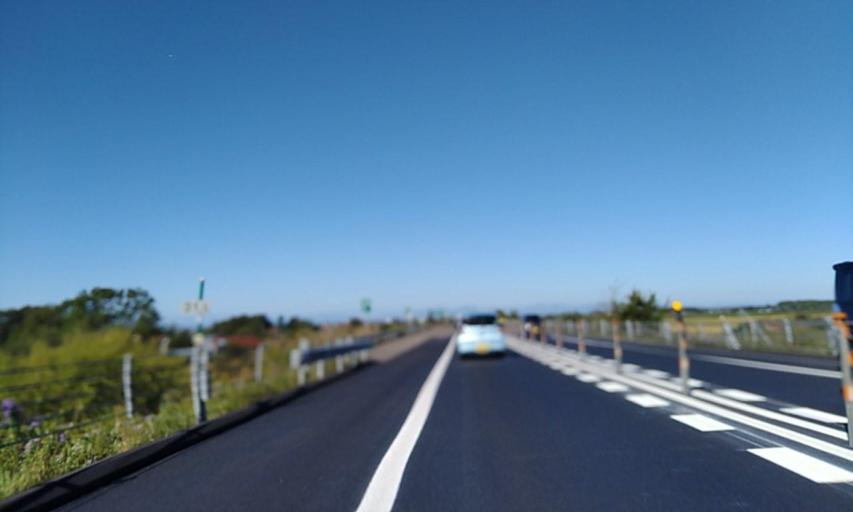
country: JP
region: Hokkaido
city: Tomakomai
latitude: 42.5780
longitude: 141.9596
